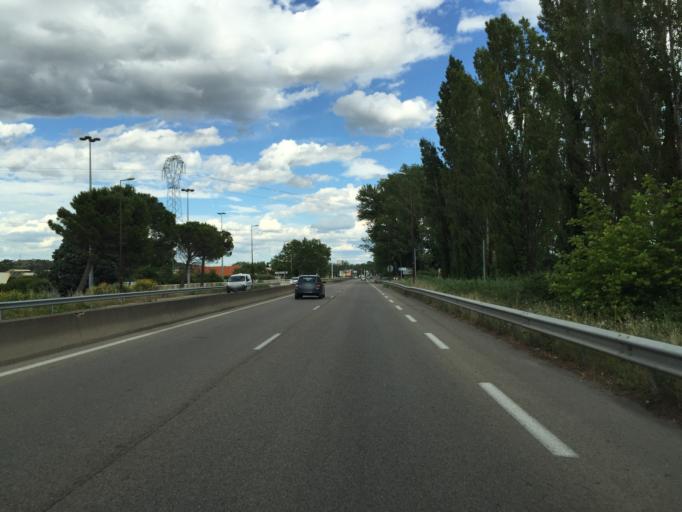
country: FR
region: Provence-Alpes-Cote d'Azur
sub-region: Departement du Vaucluse
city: Montfavet
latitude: 43.9200
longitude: 4.8636
